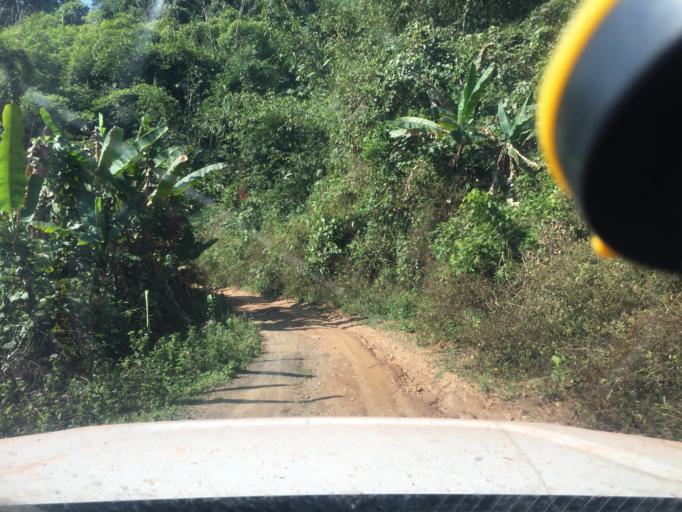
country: LA
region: Phongsali
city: Phongsali
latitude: 21.7032
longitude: 102.3921
